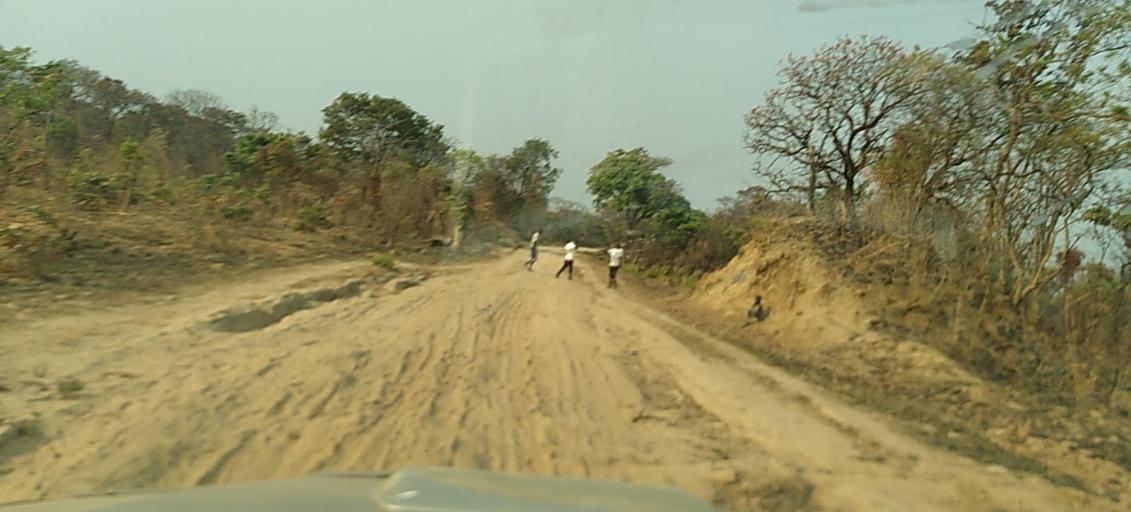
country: ZM
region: North-Western
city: Kasempa
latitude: -13.2701
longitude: 26.5586
